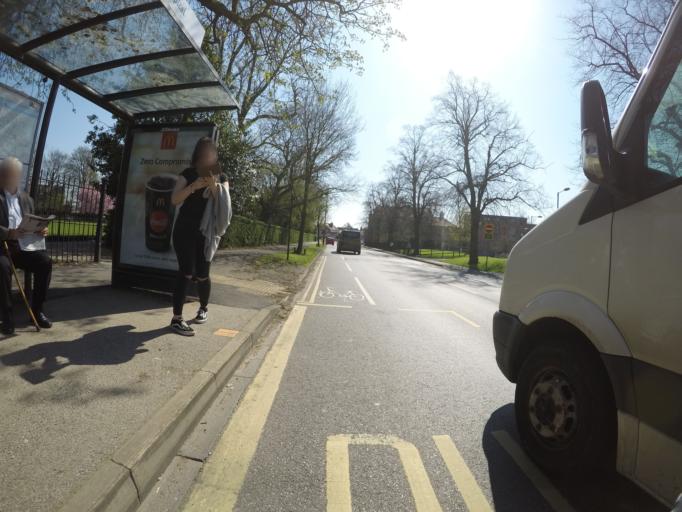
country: GB
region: England
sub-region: City of York
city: York
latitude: 53.9692
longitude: -1.0816
